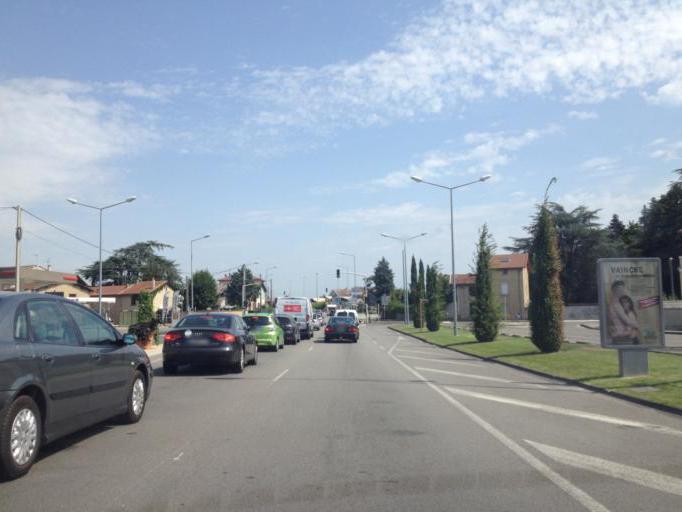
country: FR
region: Rhone-Alpes
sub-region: Departement de la Drome
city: Romans-sur-Isere
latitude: 45.0359
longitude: 5.0539
